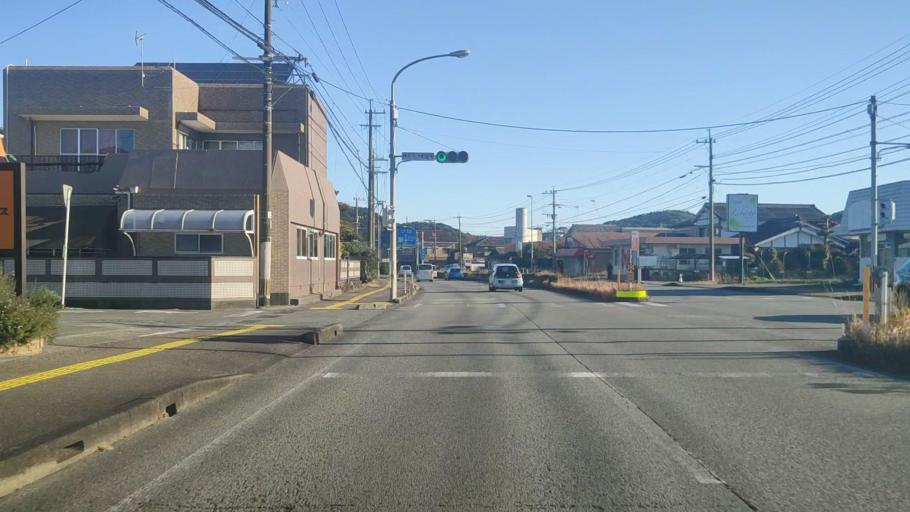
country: JP
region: Miyazaki
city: Nobeoka
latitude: 32.4854
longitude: 131.6622
